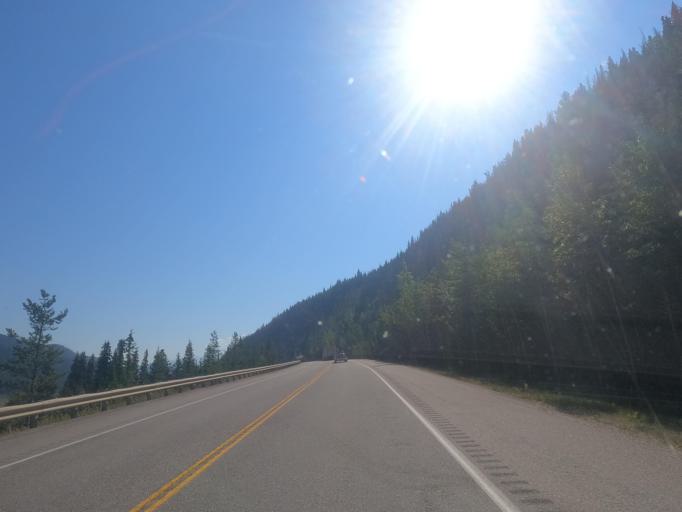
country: CA
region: Alberta
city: Jasper Park Lodge
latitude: 52.8776
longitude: -118.3429
